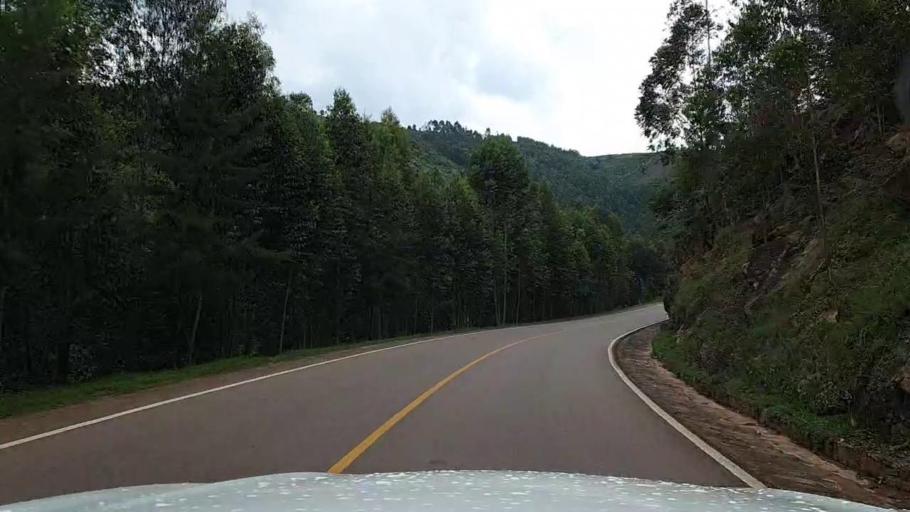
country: RW
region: Northern Province
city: Byumba
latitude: -1.7209
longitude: 30.1189
